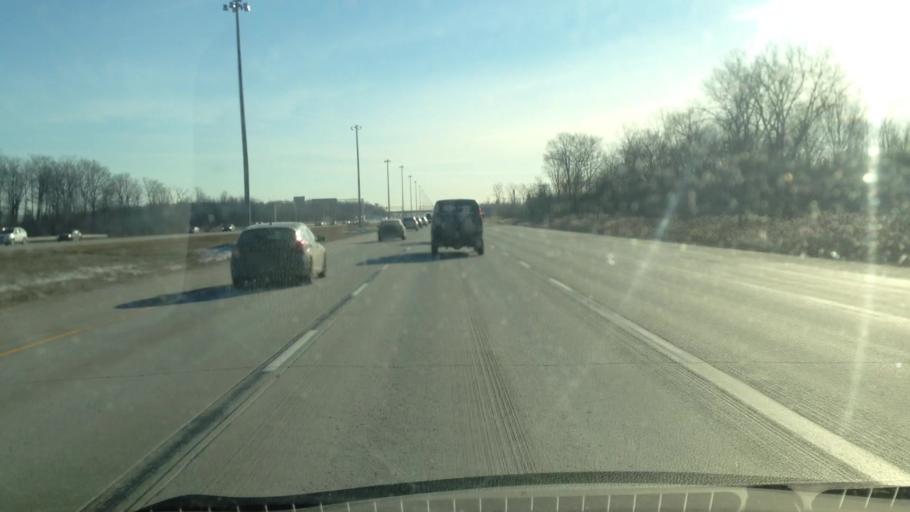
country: CA
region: Quebec
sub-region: Laurentides
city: Saint-Jerome
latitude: 45.7102
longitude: -73.9643
